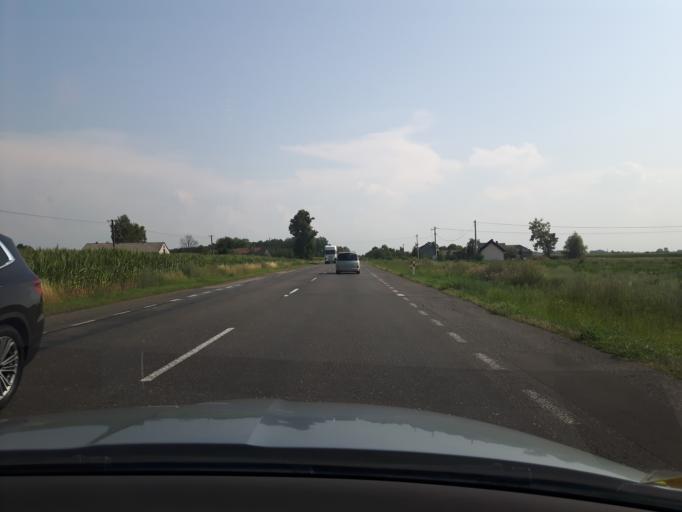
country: PL
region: Masovian Voivodeship
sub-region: Powiat plonski
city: Plonsk
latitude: 52.6700
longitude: 20.3727
